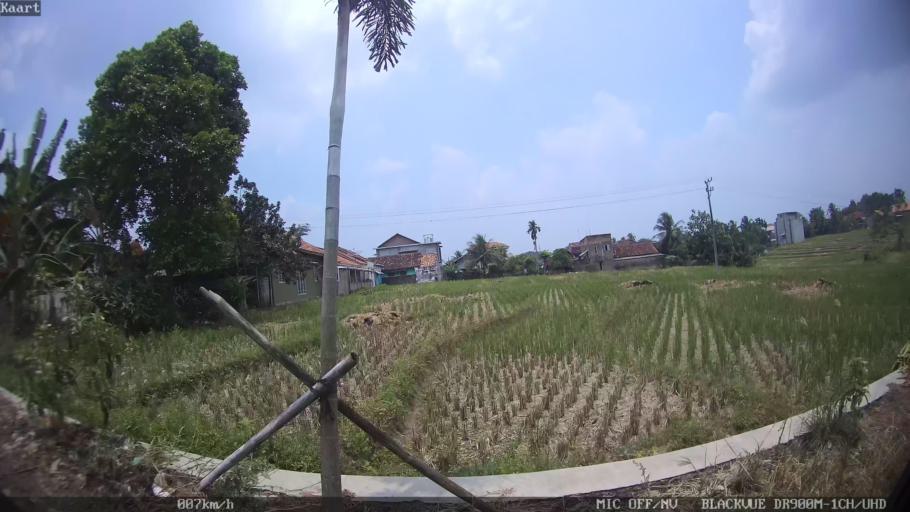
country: ID
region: Lampung
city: Pringsewu
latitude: -5.3545
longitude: 104.9623
